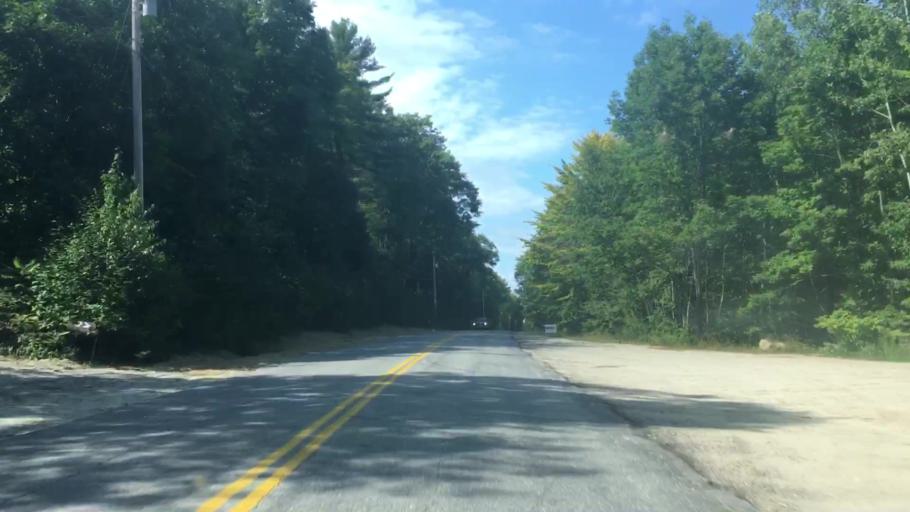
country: US
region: Maine
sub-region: Androscoggin County
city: Poland
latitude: 44.0180
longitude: -70.4223
